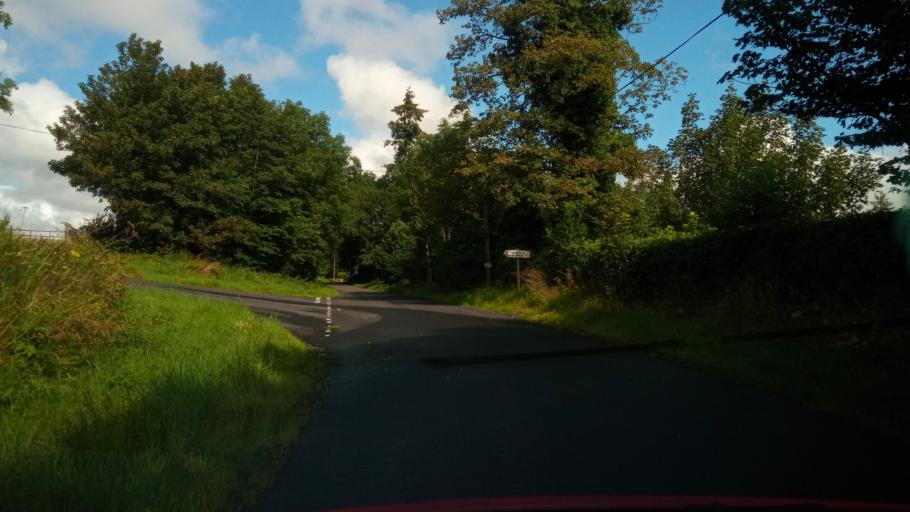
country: GB
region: Scotland
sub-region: The Scottish Borders
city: Earlston
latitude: 55.6479
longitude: -2.6998
